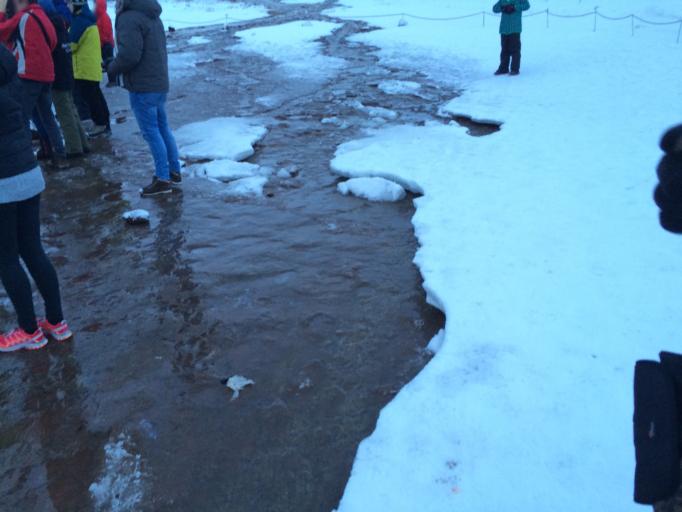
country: IS
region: South
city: Selfoss
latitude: 64.3128
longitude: -20.3004
